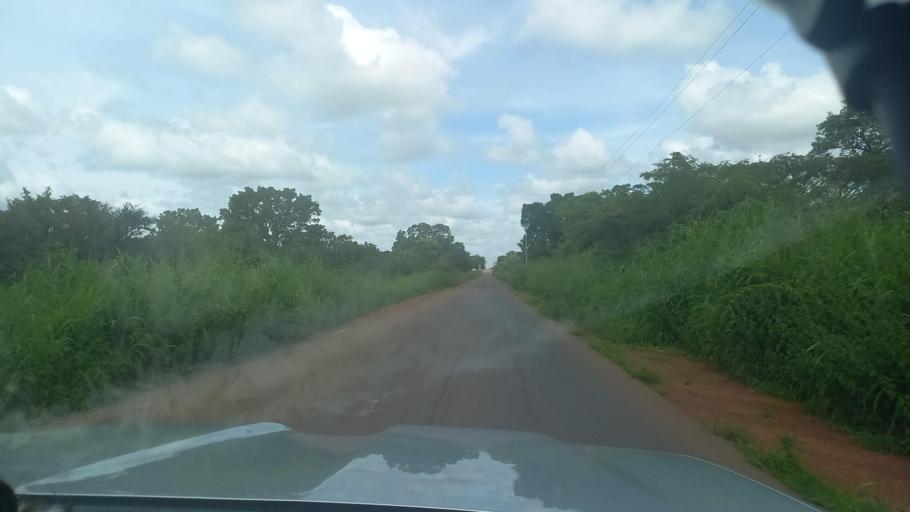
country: GM
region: Lower River
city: Kaiaf
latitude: 13.2153
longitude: -15.5440
